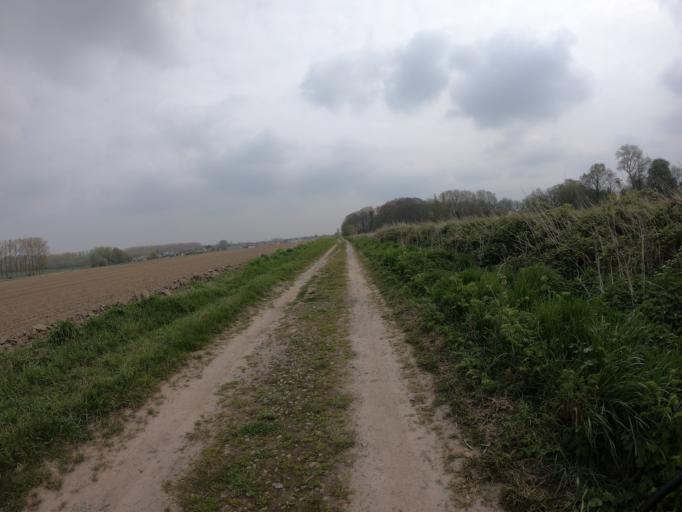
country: BE
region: Flanders
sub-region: Provincie Oost-Vlaanderen
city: Ronse
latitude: 50.7409
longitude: 3.5621
